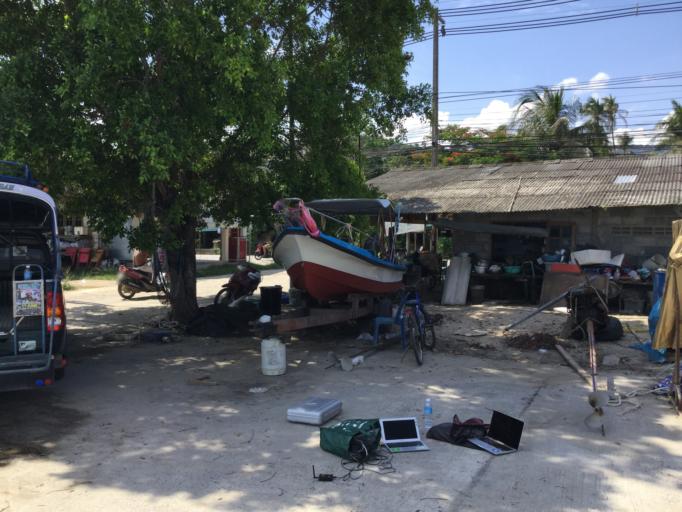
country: TH
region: Surat Thani
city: Ko Pha-Ngan
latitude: 9.7010
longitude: 100.0185
